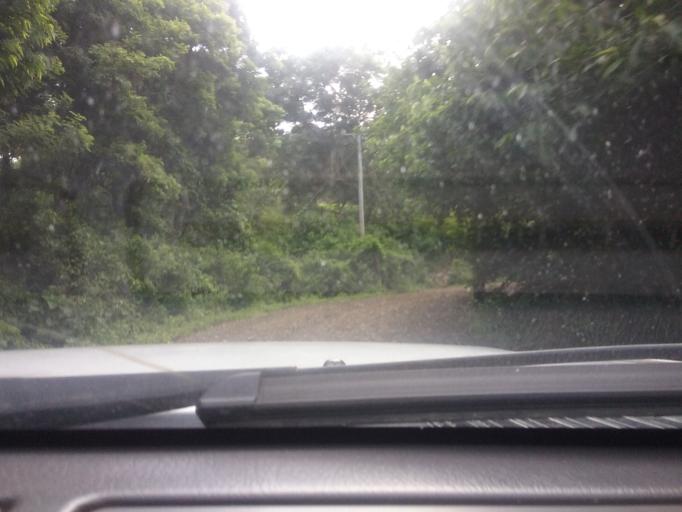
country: NI
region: Matagalpa
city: Matagalpa
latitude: 12.8813
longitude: -85.9620
